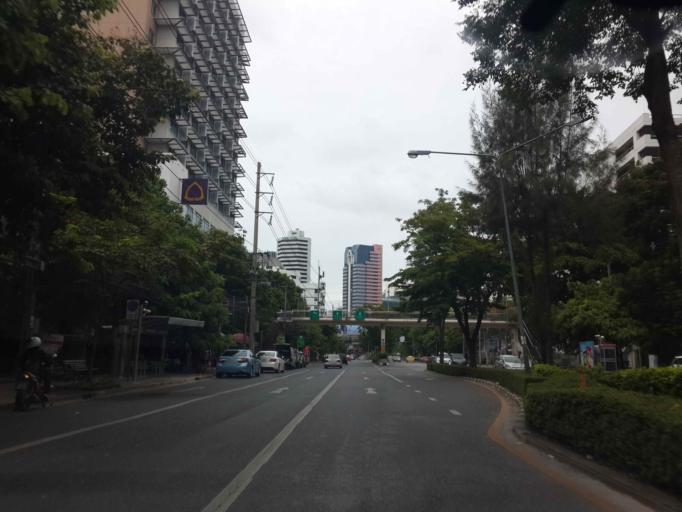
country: TH
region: Bangkok
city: Pathum Wan
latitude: 13.7348
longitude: 100.5342
